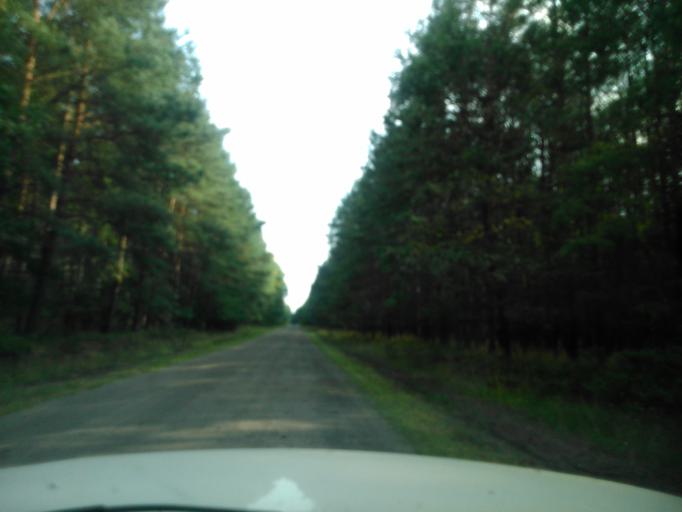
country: PL
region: Kujawsko-Pomorskie
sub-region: Powiat golubsko-dobrzynski
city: Golub-Dobrzyn
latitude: 53.1591
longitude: 19.1284
